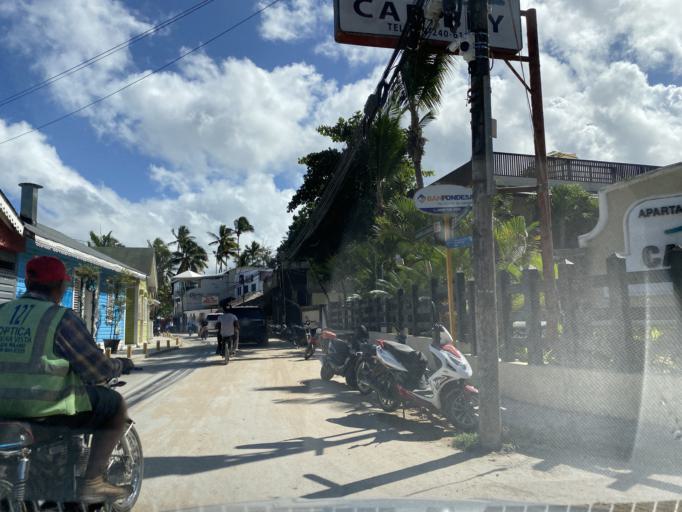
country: DO
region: Samana
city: Las Terrenas
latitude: 19.3228
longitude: -69.5419
